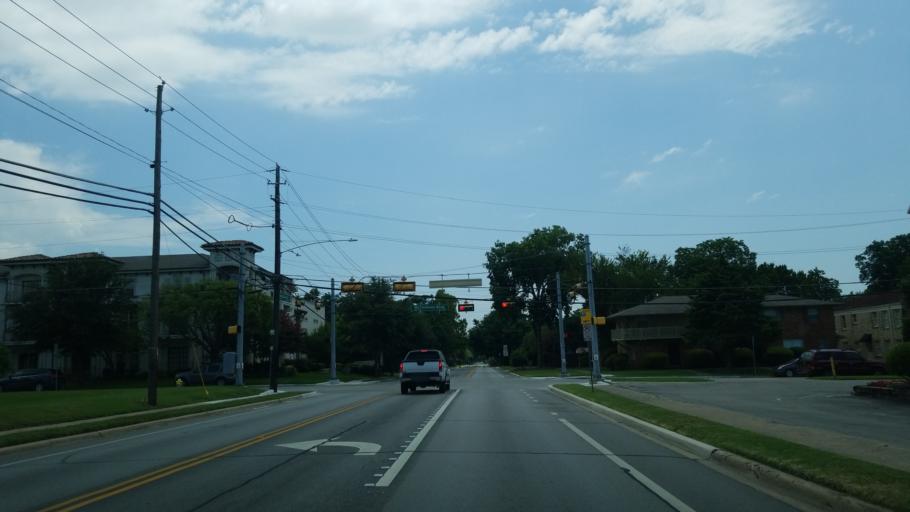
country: US
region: Texas
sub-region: Dallas County
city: Highland Park
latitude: 32.8304
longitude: -96.7680
